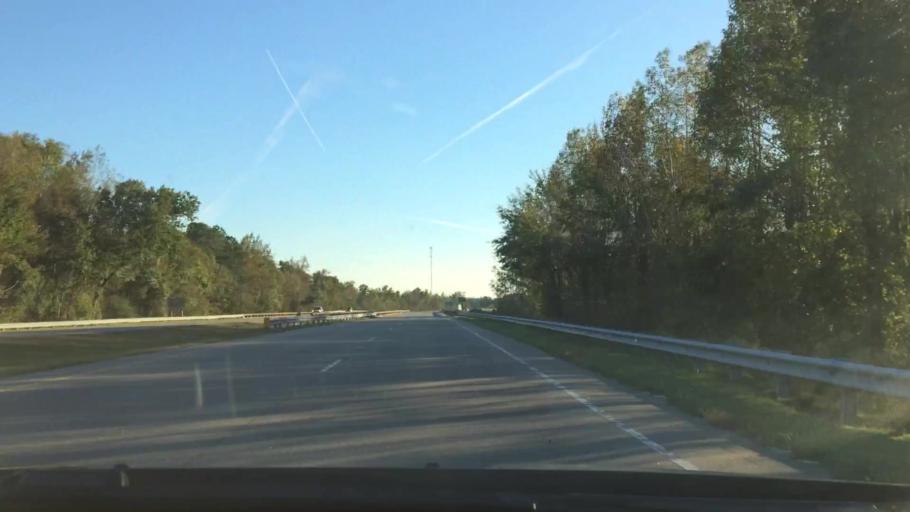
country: US
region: North Carolina
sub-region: Pitt County
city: Grifton
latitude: 35.3826
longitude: -77.4495
